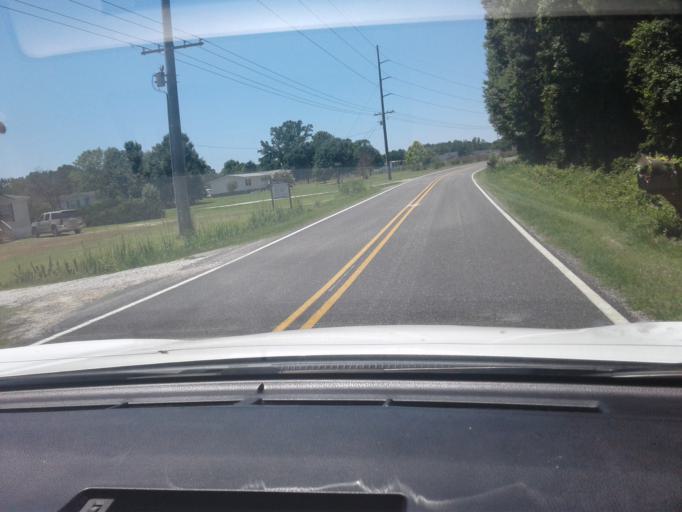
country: US
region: North Carolina
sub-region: Harnett County
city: Walkertown
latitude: 35.3383
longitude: -78.9101
